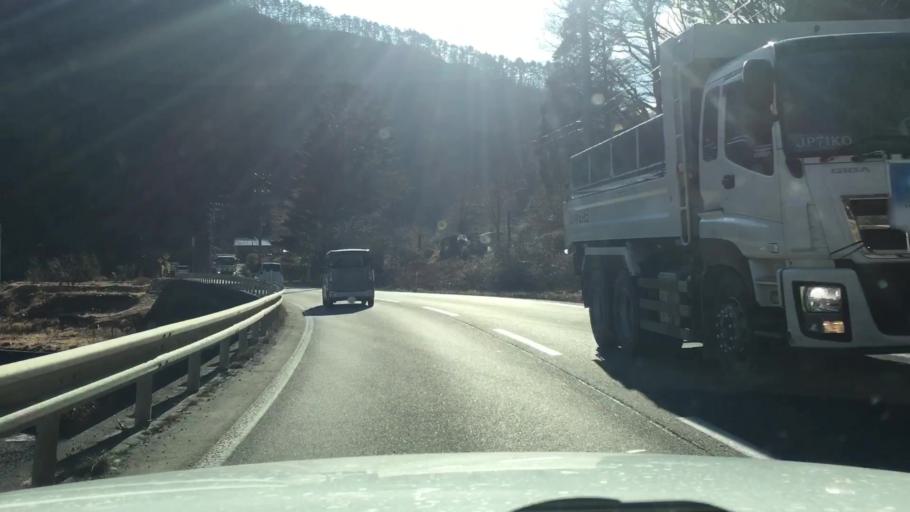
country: JP
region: Iwate
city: Miyako
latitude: 39.6086
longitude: 141.7872
